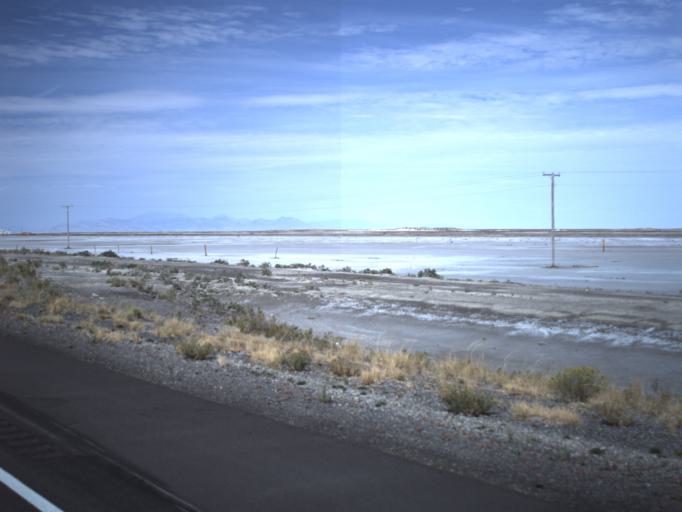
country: US
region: Utah
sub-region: Tooele County
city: Wendover
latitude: 40.7276
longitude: -113.2785
